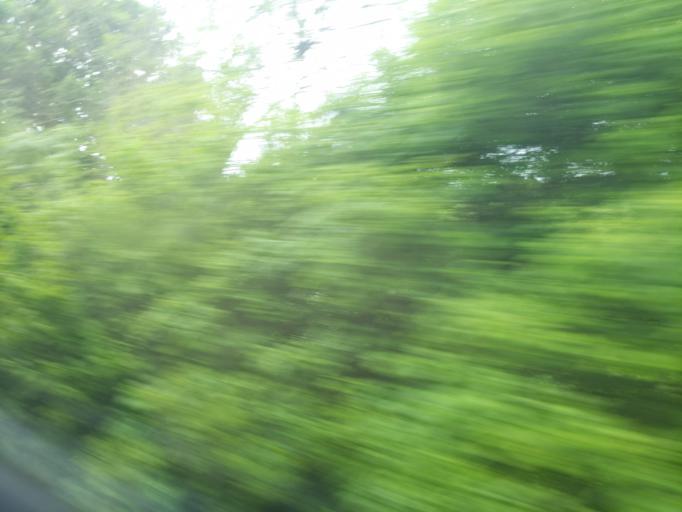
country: GB
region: England
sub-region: Devon
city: Winkleigh
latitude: 50.9042
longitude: -3.8861
